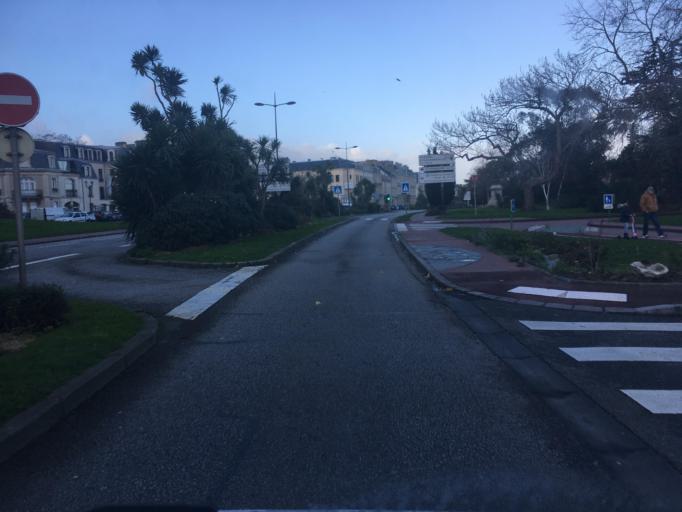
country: FR
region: Lower Normandy
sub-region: Departement de la Manche
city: Cherbourg-Octeville
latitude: 49.6424
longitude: -1.6227
